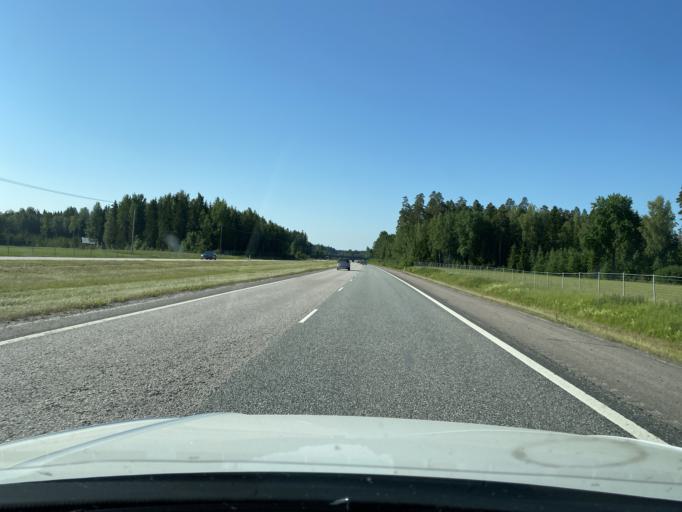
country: FI
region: Uusimaa
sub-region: Helsinki
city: Nurmijaervi
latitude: 60.4782
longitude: 24.8488
